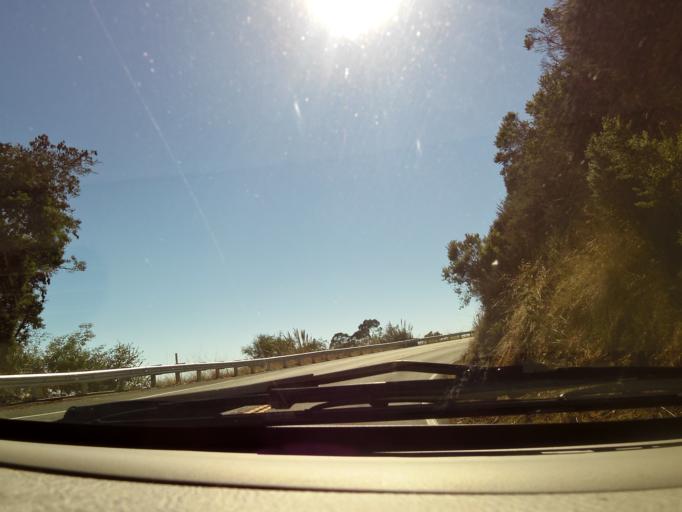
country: US
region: California
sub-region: Santa Cruz County
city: Interlaken
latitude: 36.9796
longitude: -121.7149
